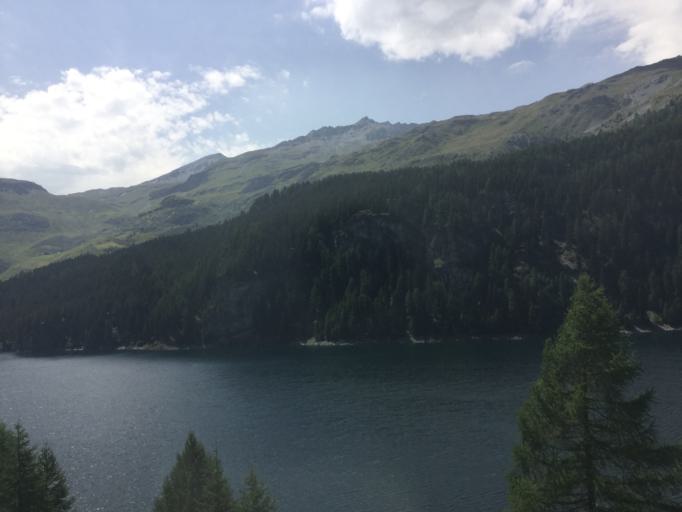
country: CH
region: Grisons
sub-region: Maloja District
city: Silvaplana
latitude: 46.4966
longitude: 9.6433
